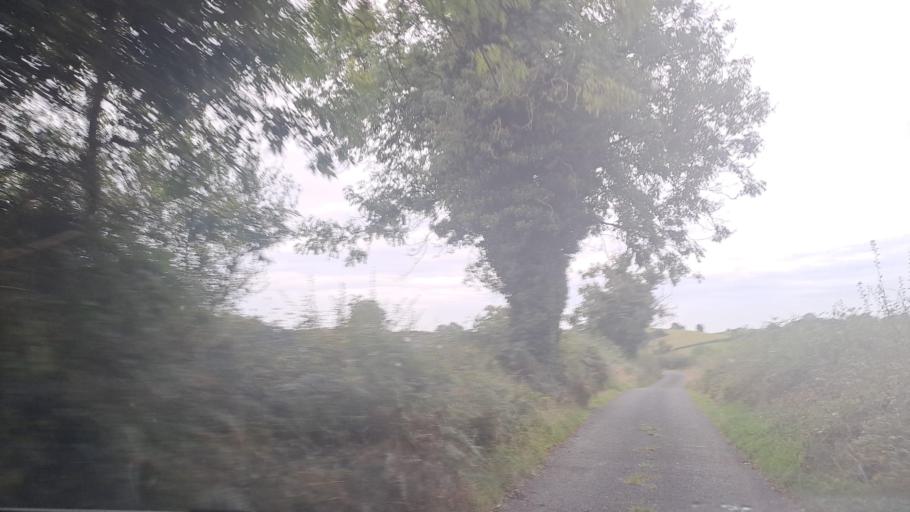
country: IE
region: Ulster
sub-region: County Monaghan
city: Carrickmacross
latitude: 53.9837
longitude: -6.7898
